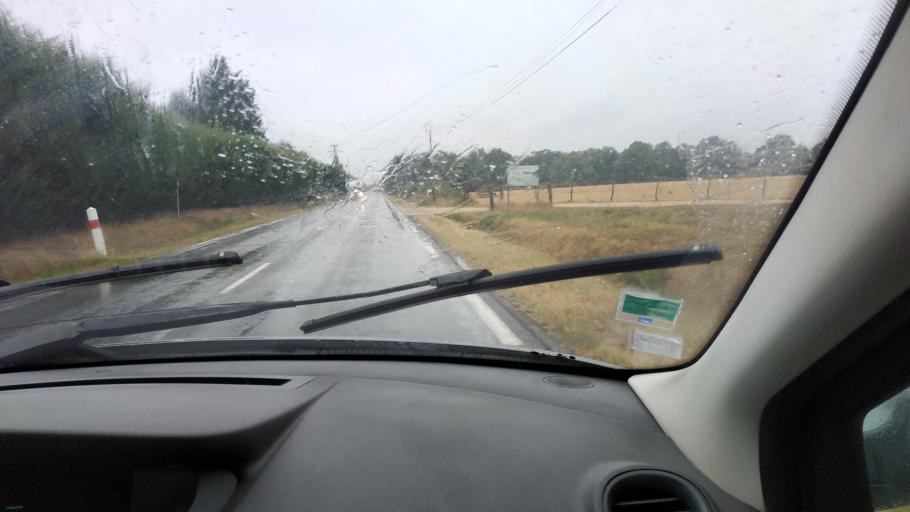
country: FR
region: Centre
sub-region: Departement du Loiret
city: Bellegarde
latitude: 47.9347
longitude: 2.3893
